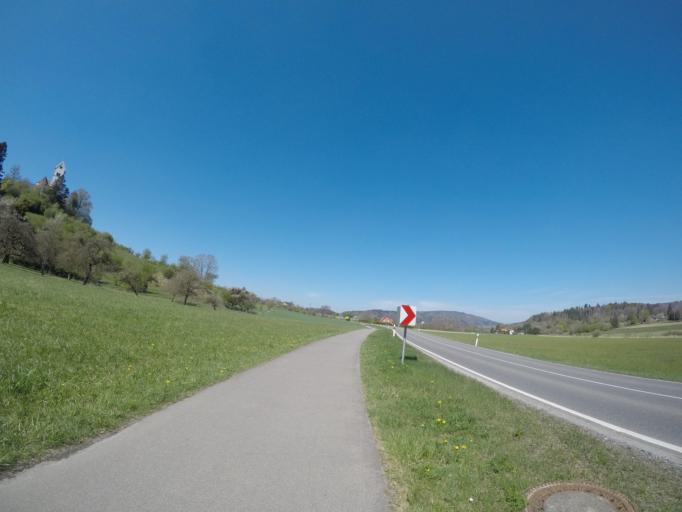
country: DE
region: Baden-Wuerttemberg
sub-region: Tuebingen Region
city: Markdorf
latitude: 47.7725
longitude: 9.4085
